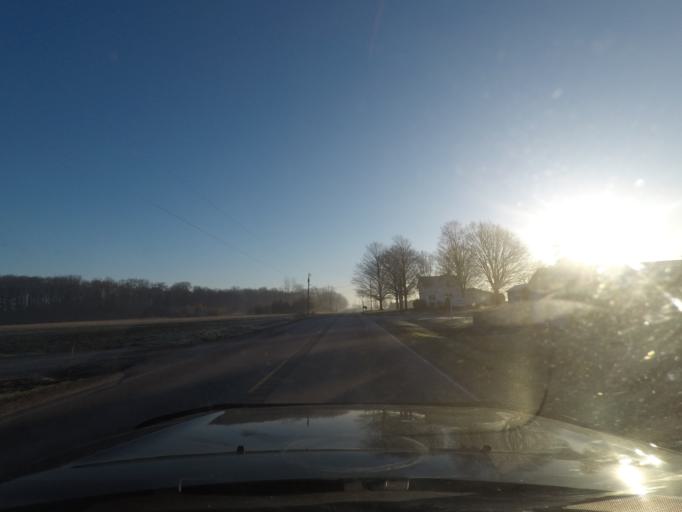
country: US
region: Indiana
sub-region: Elkhart County
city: Wakarusa
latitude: 41.5272
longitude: -85.9570
